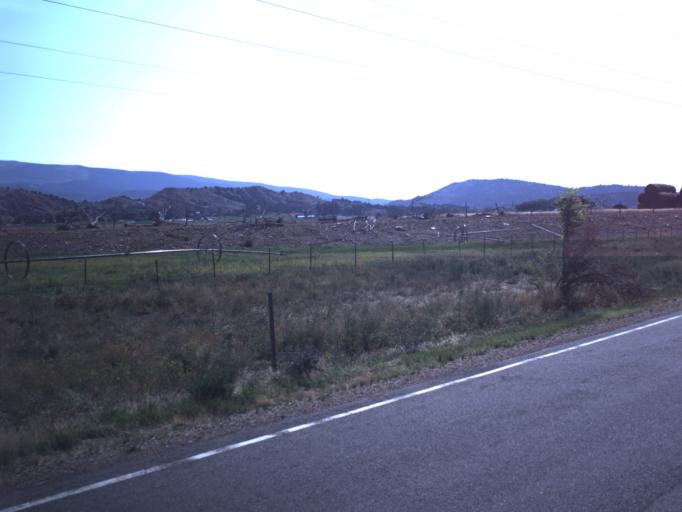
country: US
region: Utah
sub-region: Duchesne County
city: Duchesne
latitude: 40.3741
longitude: -110.7301
